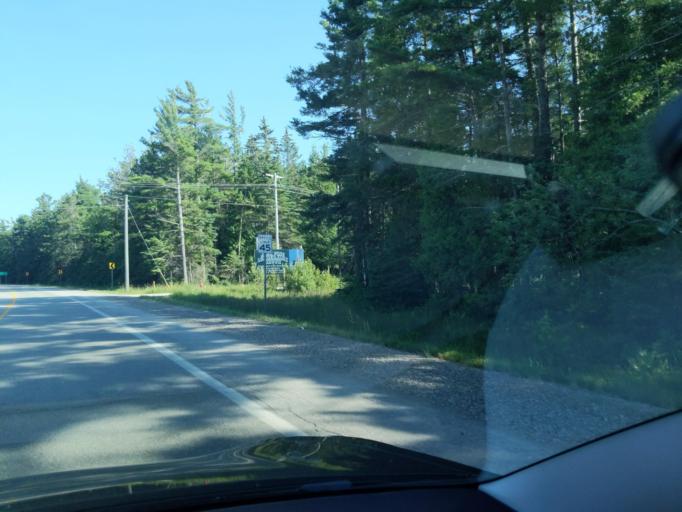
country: US
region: Michigan
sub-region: Mackinac County
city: Saint Ignace
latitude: 45.7675
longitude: -84.7249
